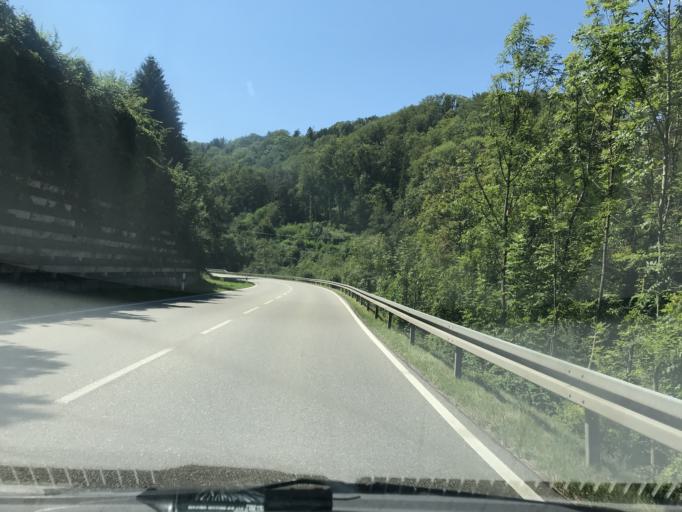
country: DE
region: Baden-Wuerttemberg
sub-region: Freiburg Region
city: Schworstadt
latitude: 47.5911
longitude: 7.9112
